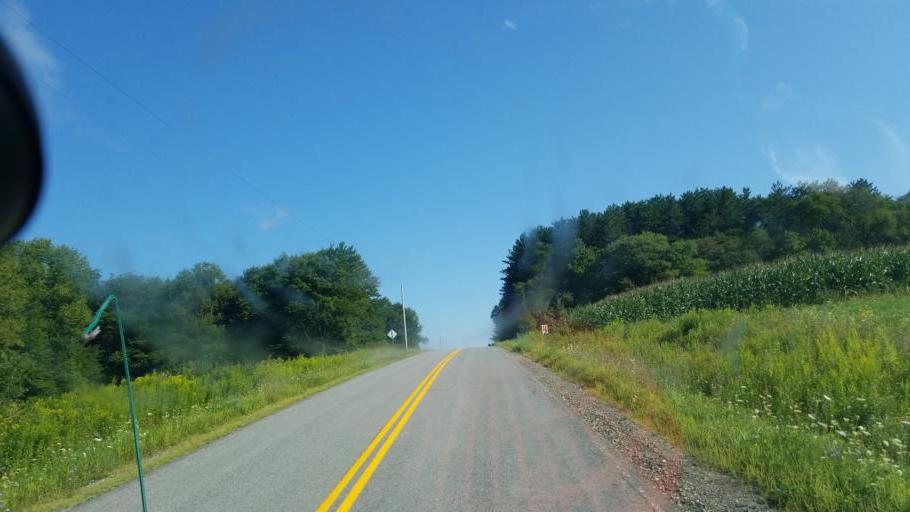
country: US
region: New York
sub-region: Allegany County
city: Andover
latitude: 42.1610
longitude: -77.7133
